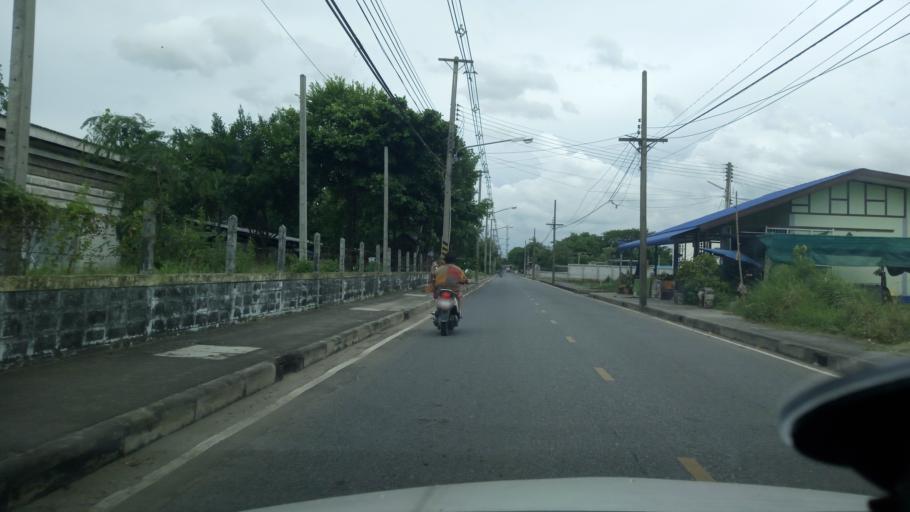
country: TH
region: Chon Buri
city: Phanat Nikhom
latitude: 13.4572
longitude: 101.1753
